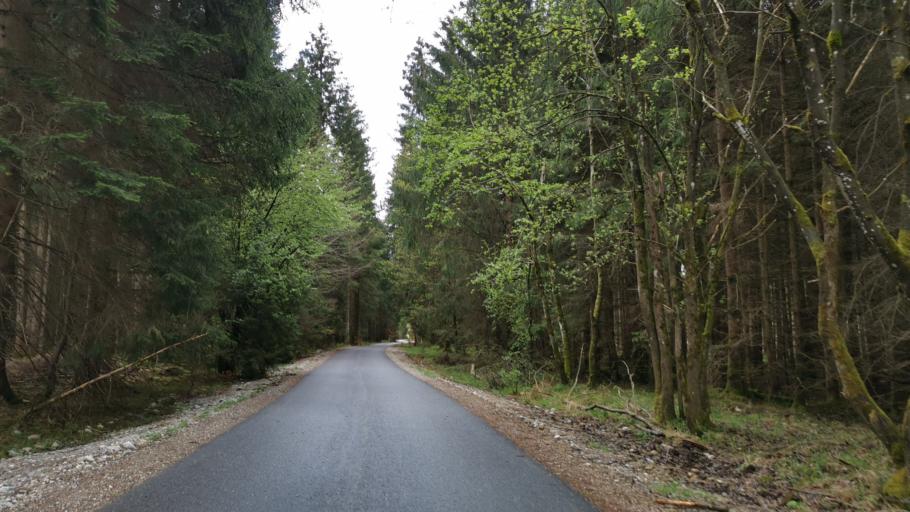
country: DE
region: Bavaria
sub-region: Upper Bavaria
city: Pullach im Isartal
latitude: 48.0667
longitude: 11.4891
